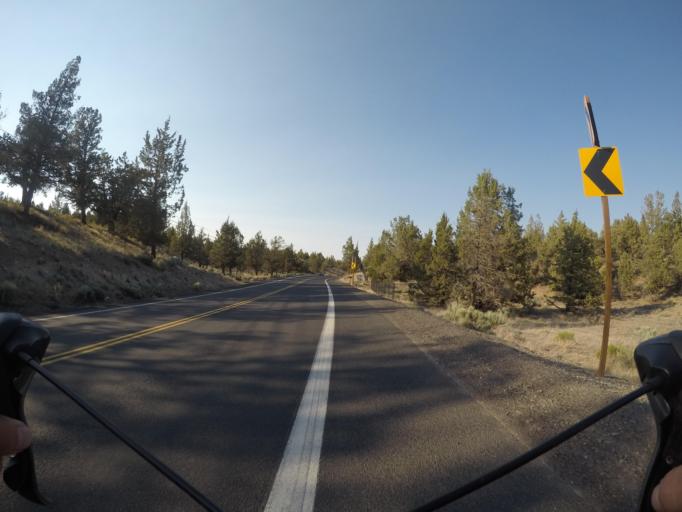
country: US
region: Oregon
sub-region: Deschutes County
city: Redmond
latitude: 44.2676
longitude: -121.2606
